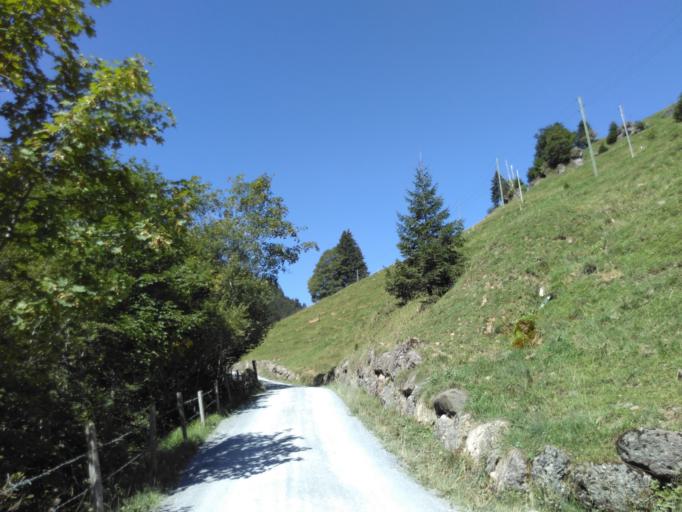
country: CH
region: Lucerne
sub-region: Lucerne-Land District
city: Vitznau
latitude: 47.0388
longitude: 8.4960
